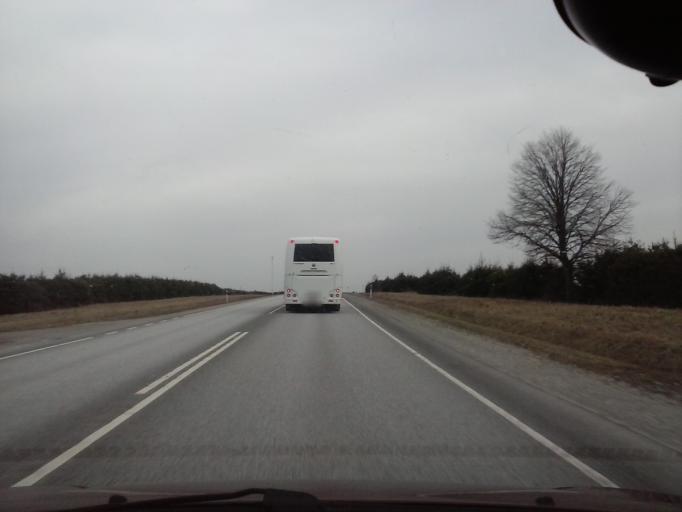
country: EE
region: Jaervamaa
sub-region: Paide linn
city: Paide
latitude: 59.0679
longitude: 25.4305
